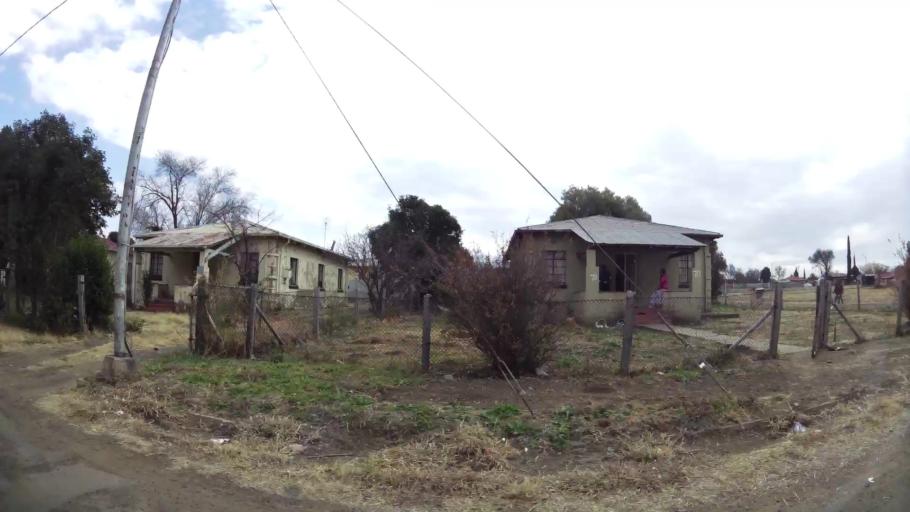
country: ZA
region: Orange Free State
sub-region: Fezile Dabi District Municipality
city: Kroonstad
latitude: -27.6542
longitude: 27.2394
